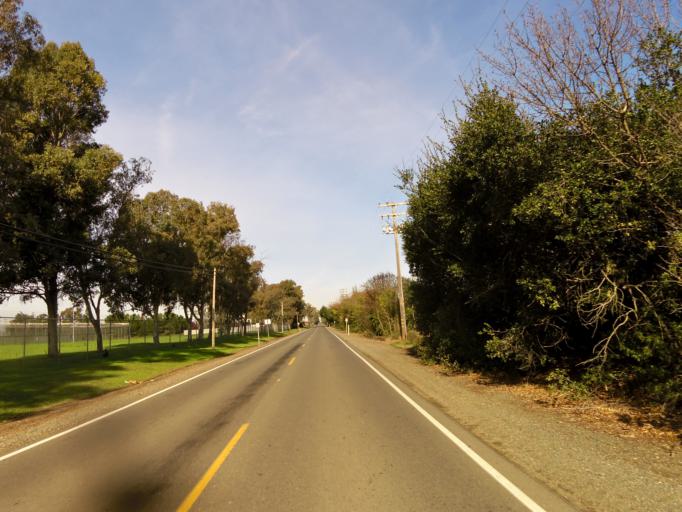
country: US
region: California
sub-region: San Joaquin County
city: Thornton
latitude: 38.3071
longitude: -121.4201
